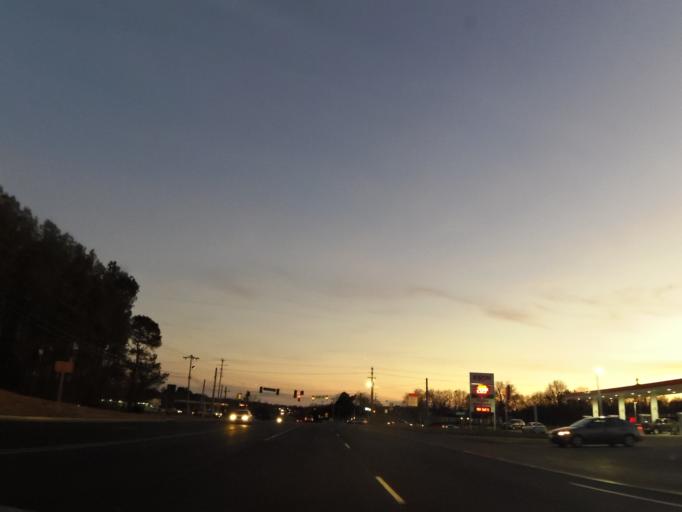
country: US
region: Georgia
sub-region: Whitfield County
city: Varnell
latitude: 34.8957
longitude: -84.9470
